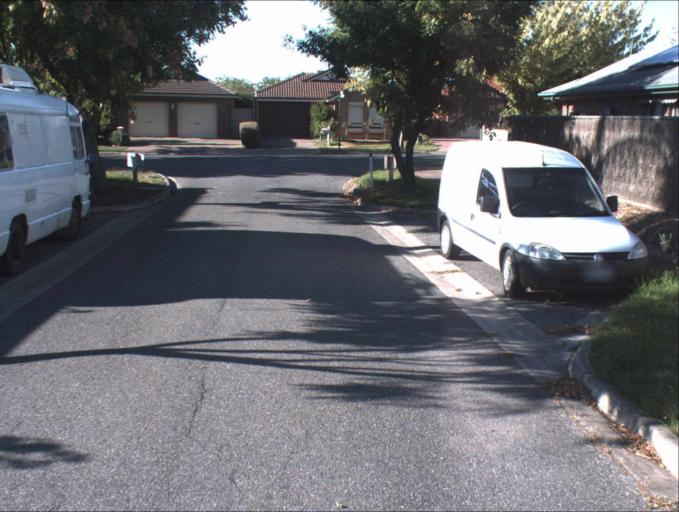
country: AU
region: South Australia
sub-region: Port Adelaide Enfield
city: Gilles Plains
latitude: -34.8554
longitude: 138.6461
